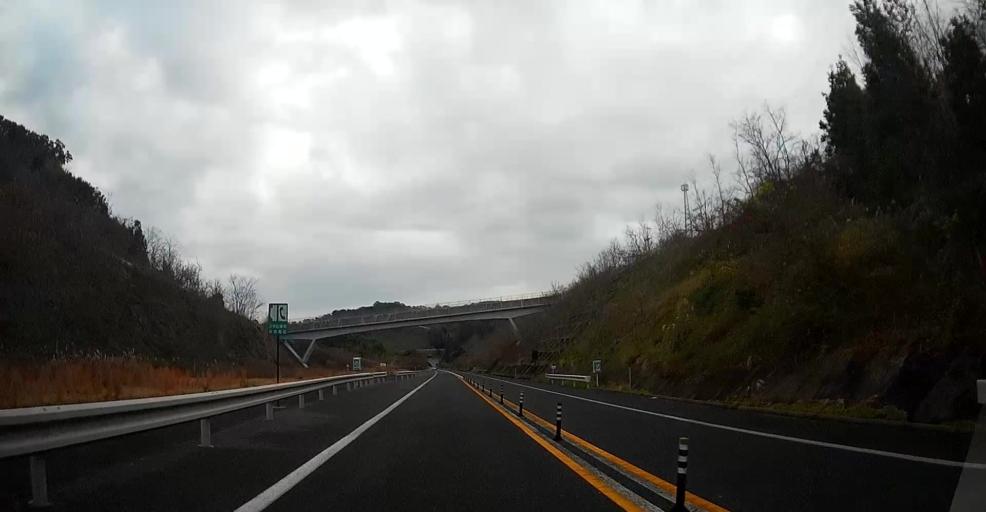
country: JP
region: Kumamoto
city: Hondo
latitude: 32.5087
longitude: 130.3293
